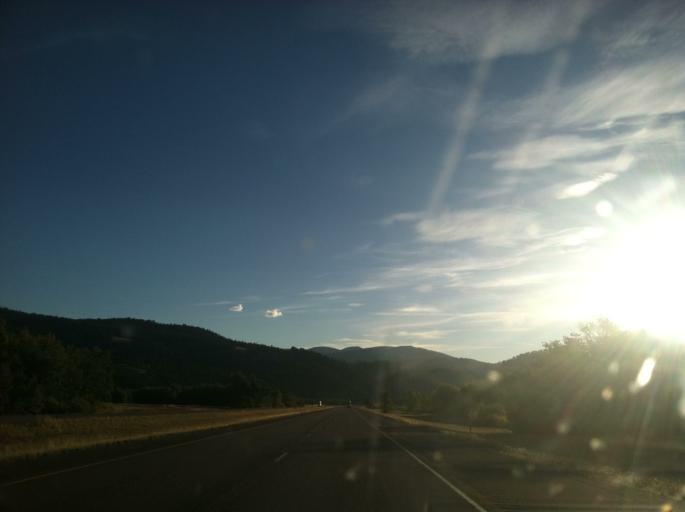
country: US
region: Montana
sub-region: Granite County
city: Philipsburg
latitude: 46.7019
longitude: -113.3433
